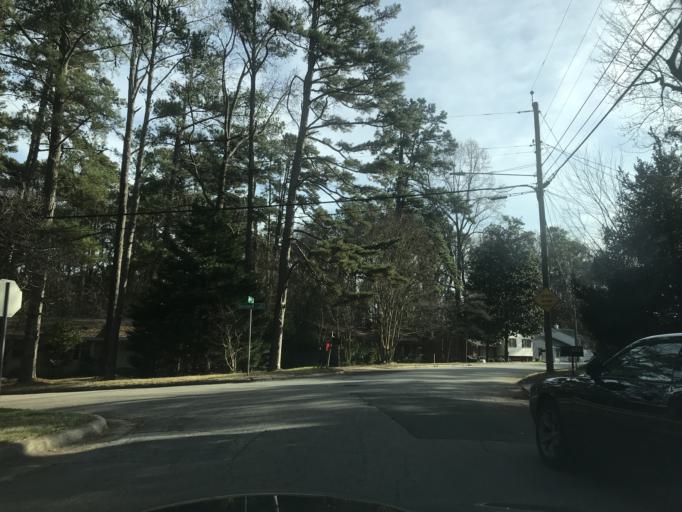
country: US
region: North Carolina
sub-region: Wake County
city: Raleigh
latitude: 35.8212
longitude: -78.5996
